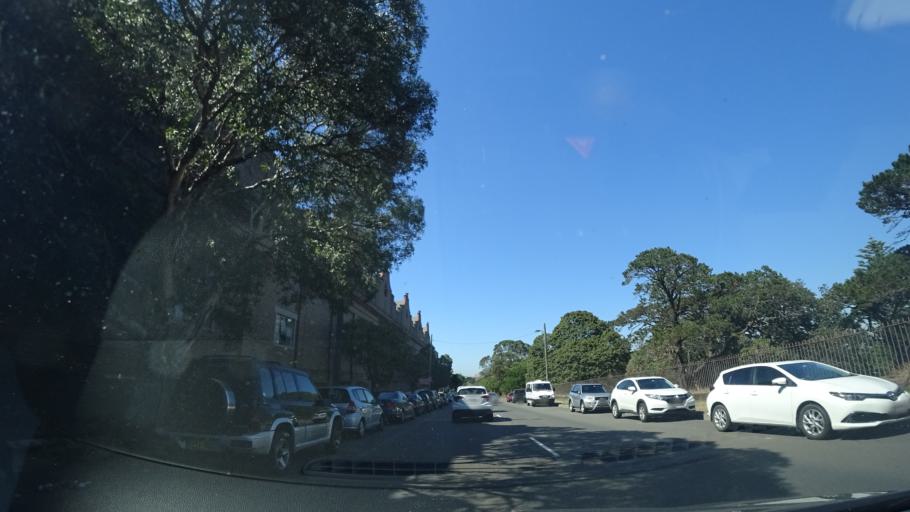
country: AU
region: New South Wales
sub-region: Waverley
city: Bondi Junction
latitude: -33.8918
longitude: 151.2416
